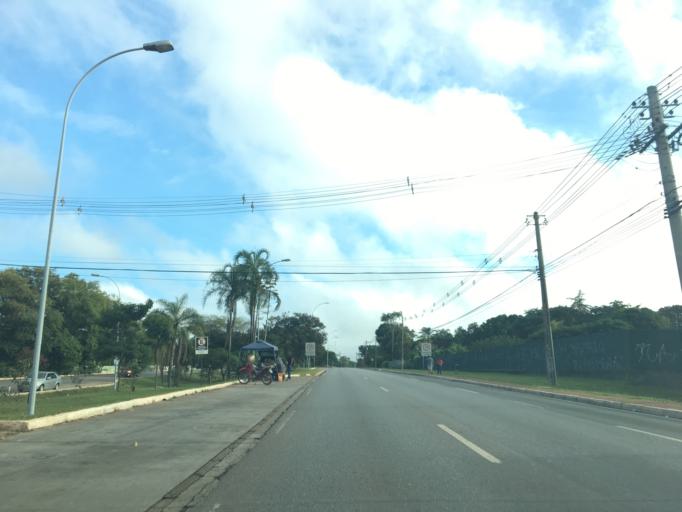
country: BR
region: Federal District
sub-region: Brasilia
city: Brasilia
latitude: -15.8203
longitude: -47.8051
